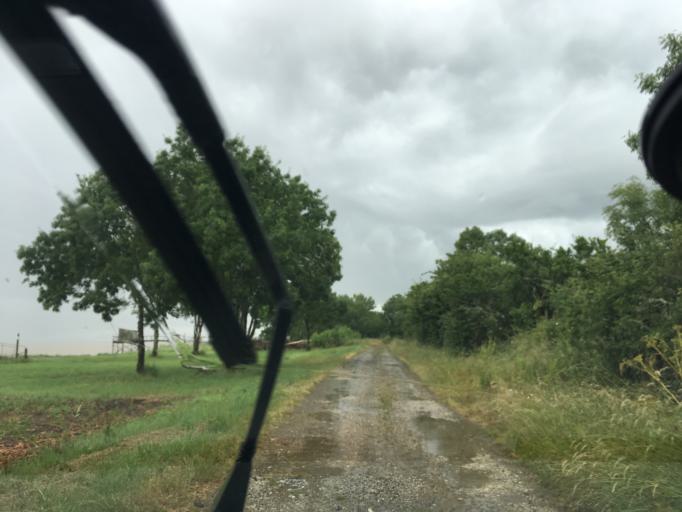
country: FR
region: Aquitaine
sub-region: Departement de la Gironde
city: Saint-Estephe
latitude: 45.3344
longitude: -0.7974
